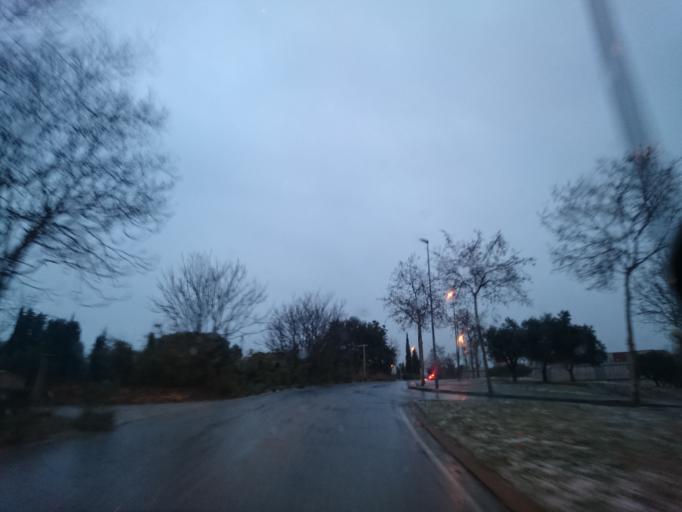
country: ES
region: Catalonia
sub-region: Provincia de Barcelona
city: Vilanova i la Geltru
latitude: 41.2403
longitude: 1.7253
